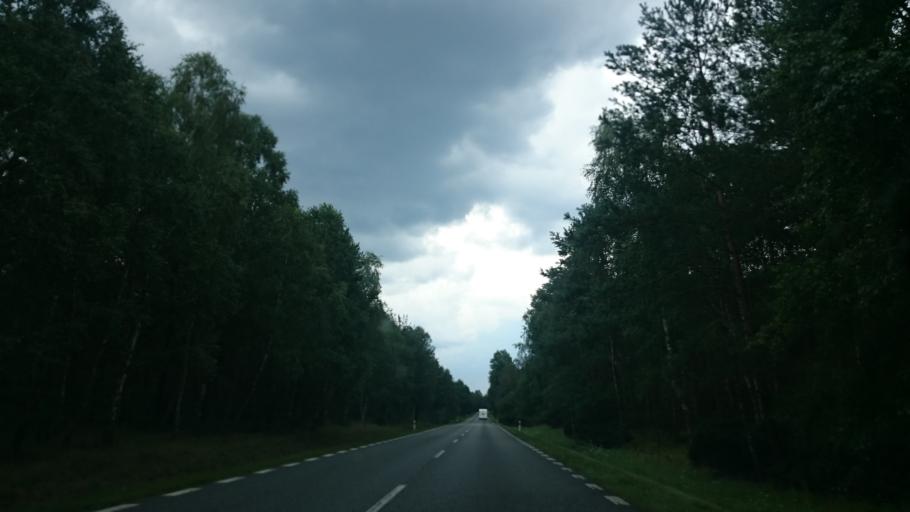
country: PL
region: Kujawsko-Pomorskie
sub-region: Powiat tucholski
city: Lubiewo
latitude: 53.4950
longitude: 18.0729
